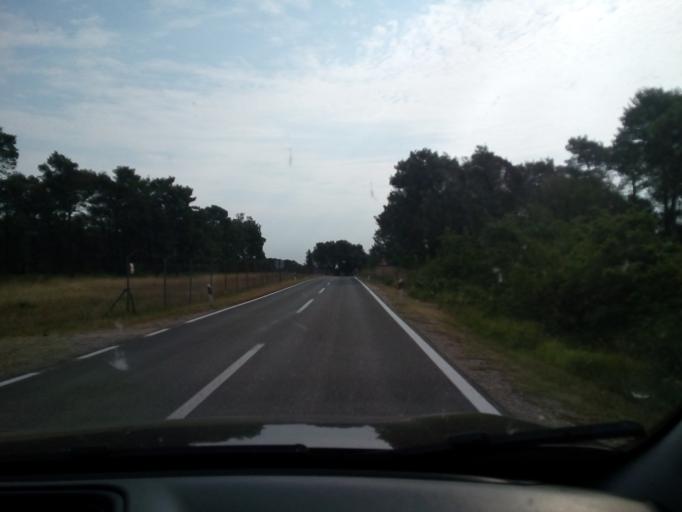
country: HR
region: Zadarska
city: Bibinje
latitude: 44.0944
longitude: 15.3258
